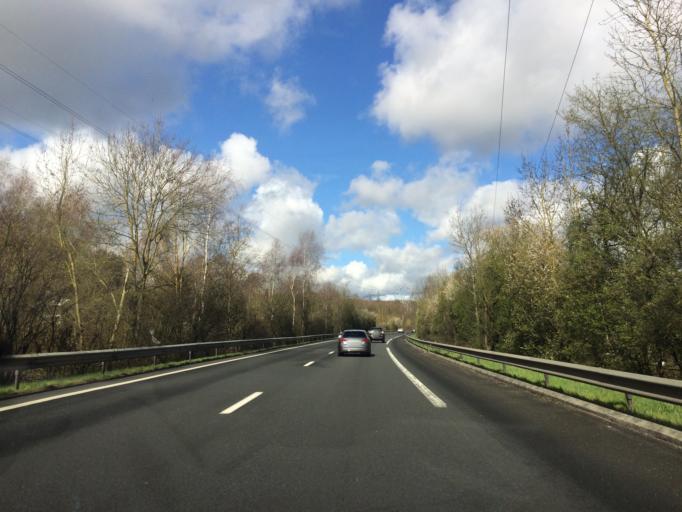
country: FR
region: Ile-de-France
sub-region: Departement de l'Essonne
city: Marcoussis
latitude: 48.6370
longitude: 2.2064
